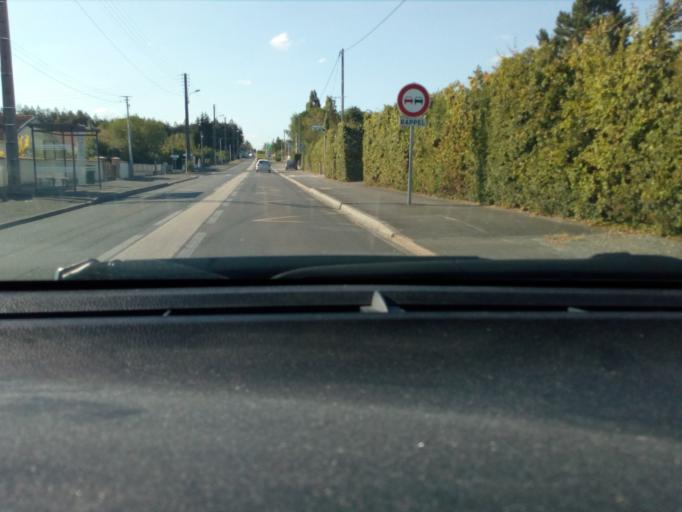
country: FR
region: Poitou-Charentes
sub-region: Departement de la Charente
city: Saint-Yrieix-sur-Charente
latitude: 45.6705
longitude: 0.1290
